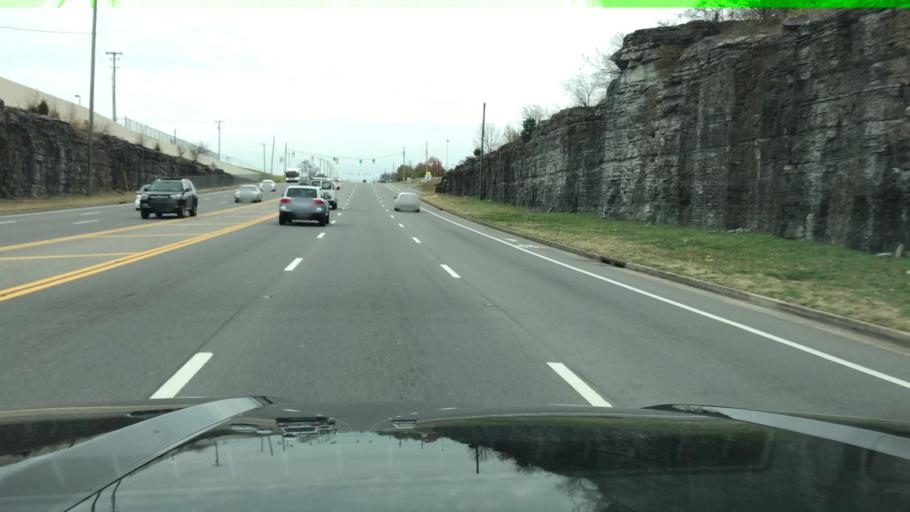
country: US
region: Tennessee
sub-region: Davidson County
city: Oak Hill
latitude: 36.1100
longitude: -86.6824
